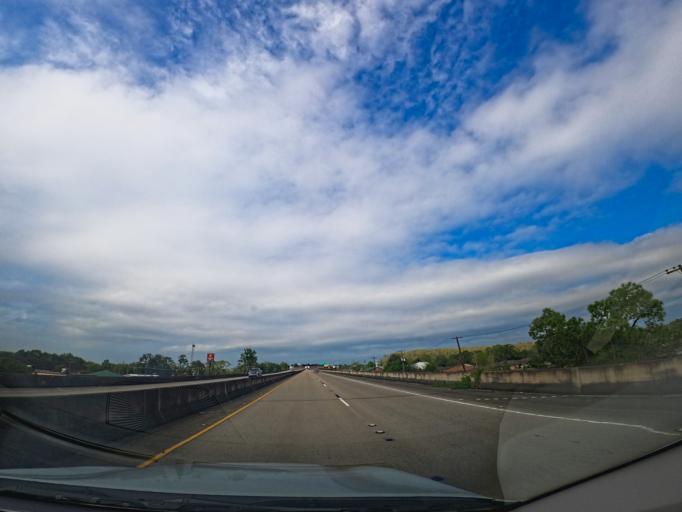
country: US
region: Louisiana
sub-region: Saint Mary Parish
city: Morgan City
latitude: 29.6967
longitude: -91.1749
